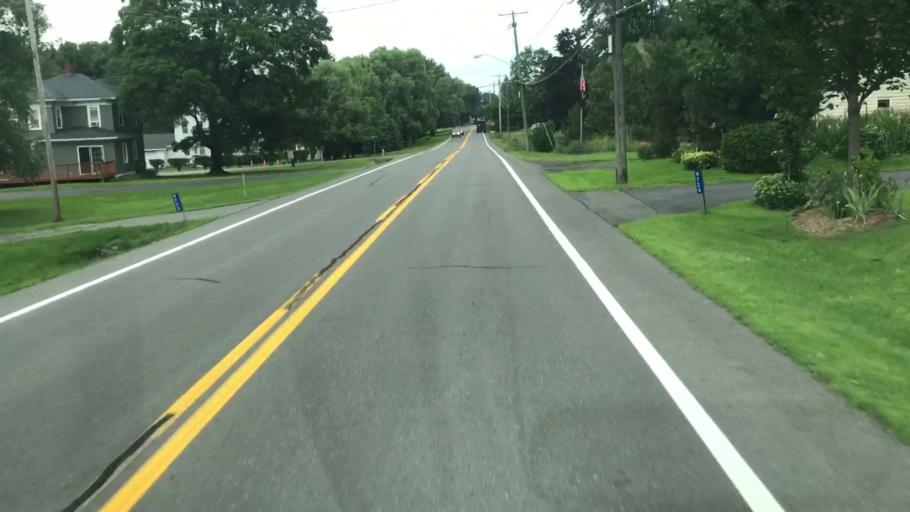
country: US
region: New York
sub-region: Onondaga County
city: Elbridge
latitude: 42.9998
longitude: -76.4575
